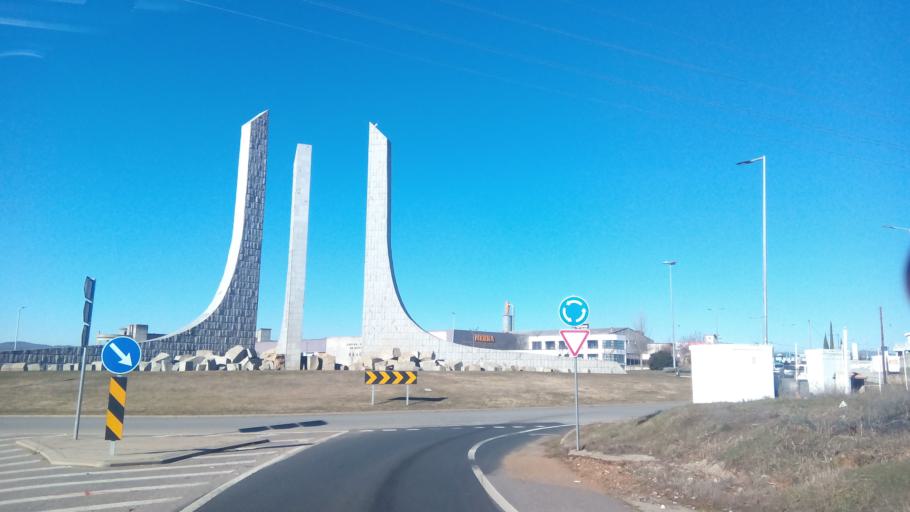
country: PT
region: Braganca
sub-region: Braganca Municipality
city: Braganca
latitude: 41.7785
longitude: -6.7789
